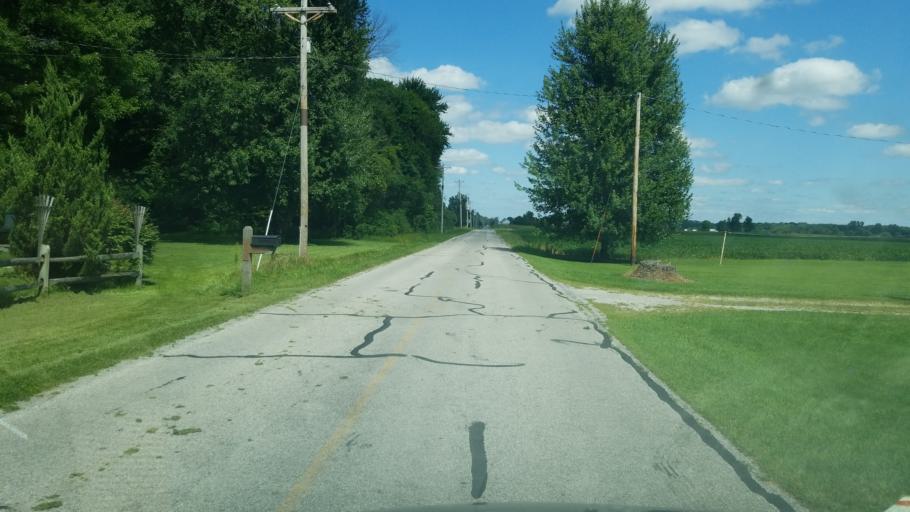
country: US
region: Ohio
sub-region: Henry County
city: Liberty Center
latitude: 41.5014
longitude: -83.9413
